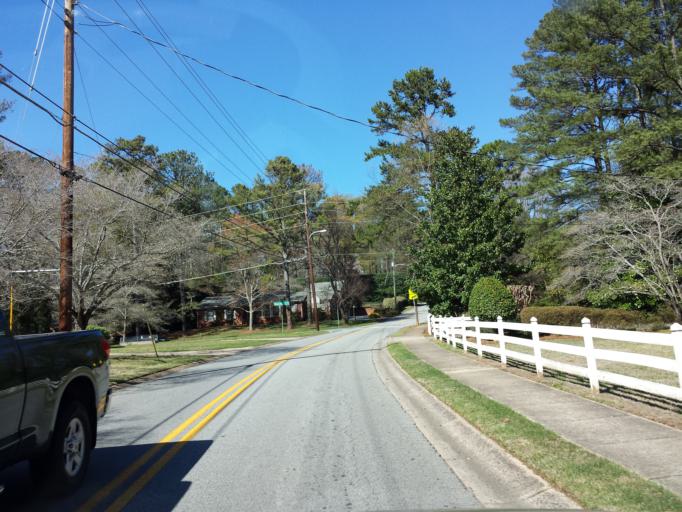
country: US
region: Georgia
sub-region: Cobb County
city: Marietta
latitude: 33.9378
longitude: -84.5667
